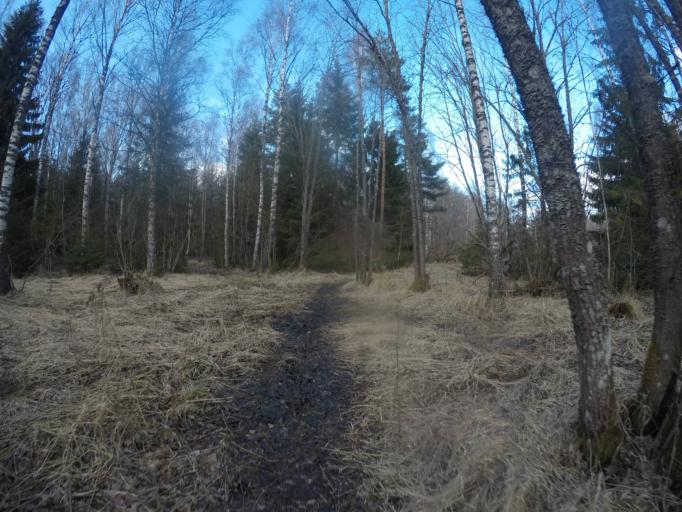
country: SE
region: Soedermanland
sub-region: Eskilstuna Kommun
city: Hallbybrunn
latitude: 59.3910
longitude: 16.4022
